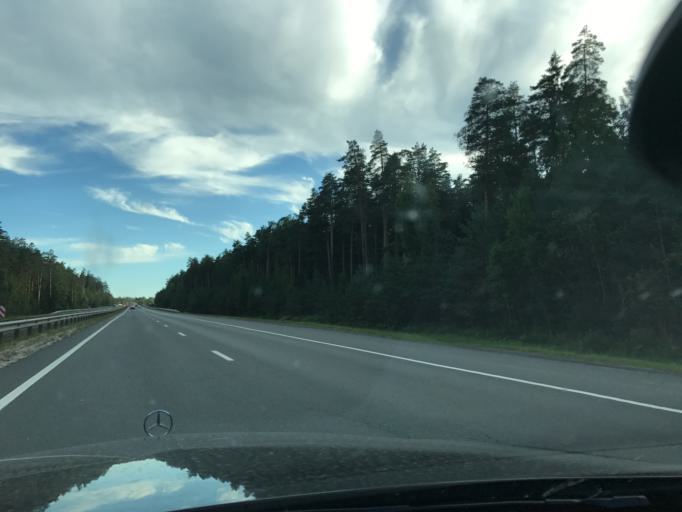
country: RU
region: Vladimir
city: Kommunar
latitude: 56.0709
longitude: 40.4640
